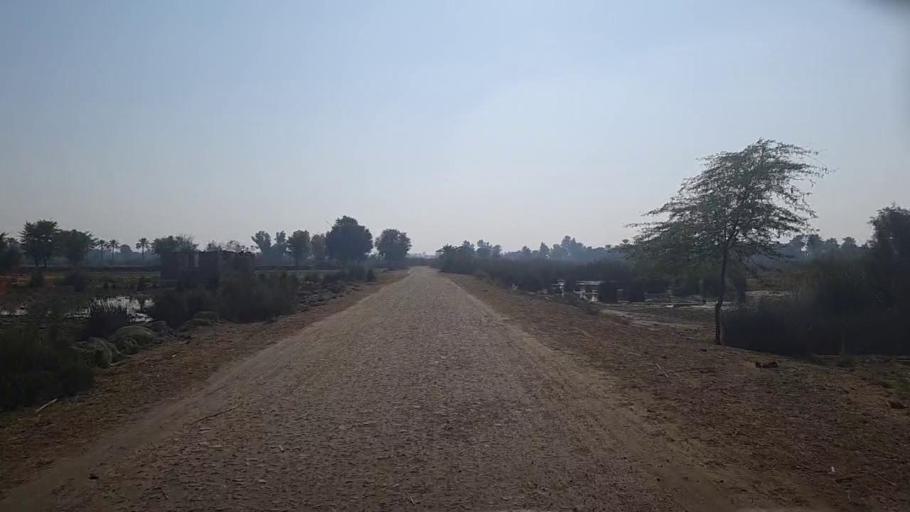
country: PK
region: Sindh
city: Kot Diji
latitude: 27.4265
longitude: 68.7373
